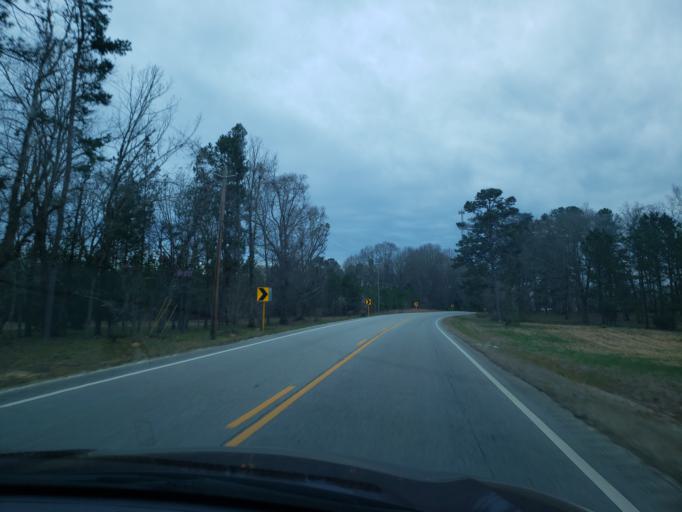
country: US
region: Alabama
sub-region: Chambers County
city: Lafayette
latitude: 32.9888
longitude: -85.4017
